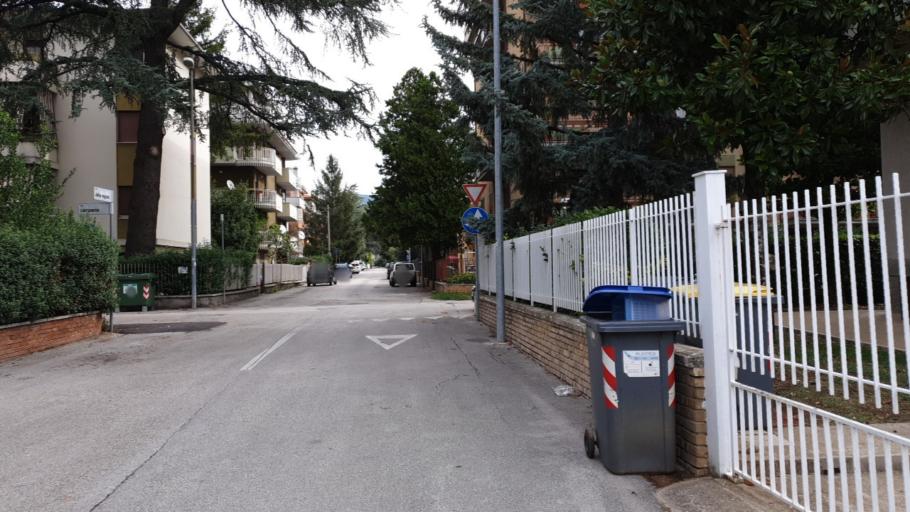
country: IT
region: Umbria
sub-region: Provincia di Perugia
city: Foligno
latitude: 42.9610
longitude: 12.7114
